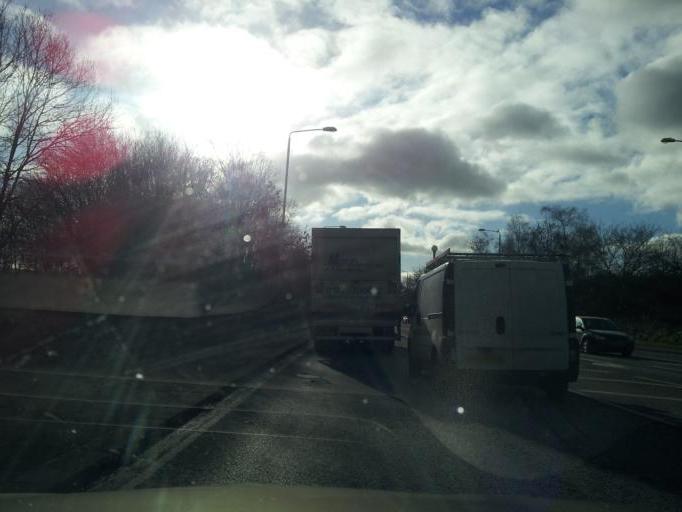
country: GB
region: England
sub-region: Nottinghamshire
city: Sutton in Ashfield
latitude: 53.1207
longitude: -1.2508
